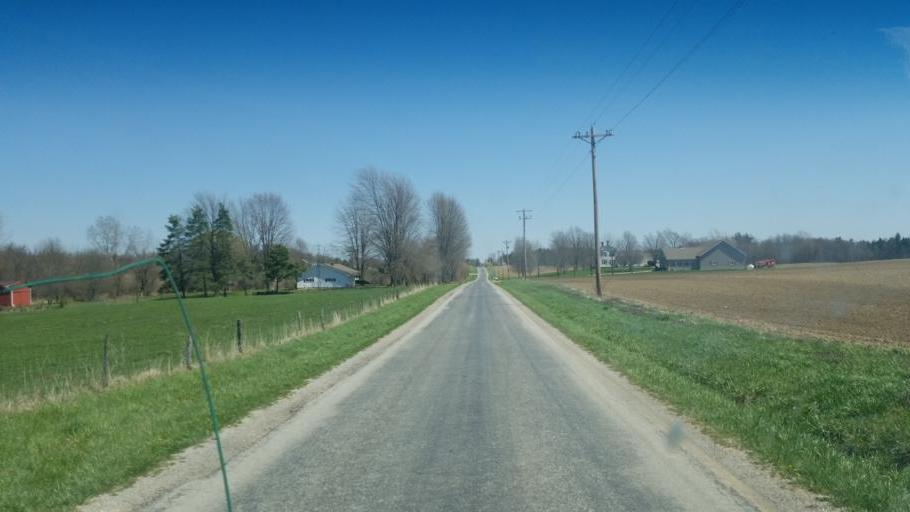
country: US
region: Ohio
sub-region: Huron County
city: Greenwich
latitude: 41.0481
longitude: -82.5076
